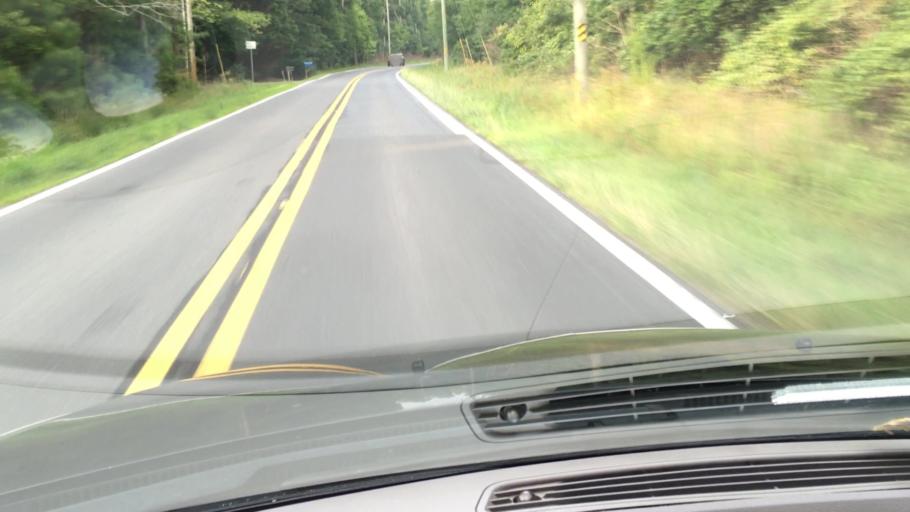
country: US
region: Delaware
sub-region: Sussex County
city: Ocean View
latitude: 38.5084
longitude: -75.1133
